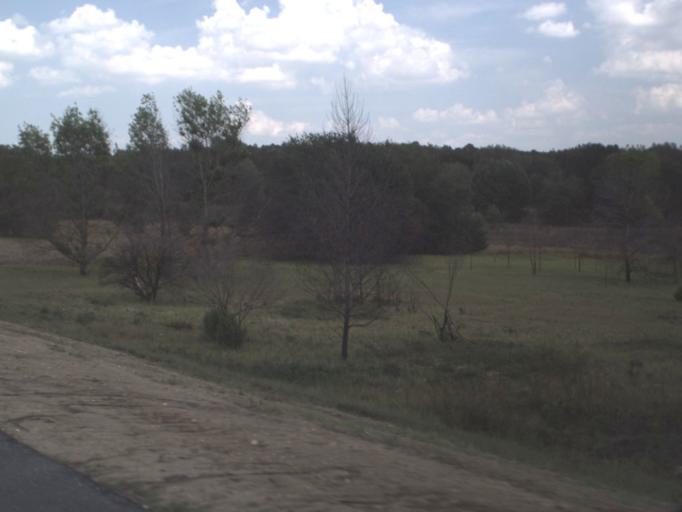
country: US
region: Florida
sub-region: Lake County
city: Groveland
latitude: 28.6320
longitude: -81.8193
